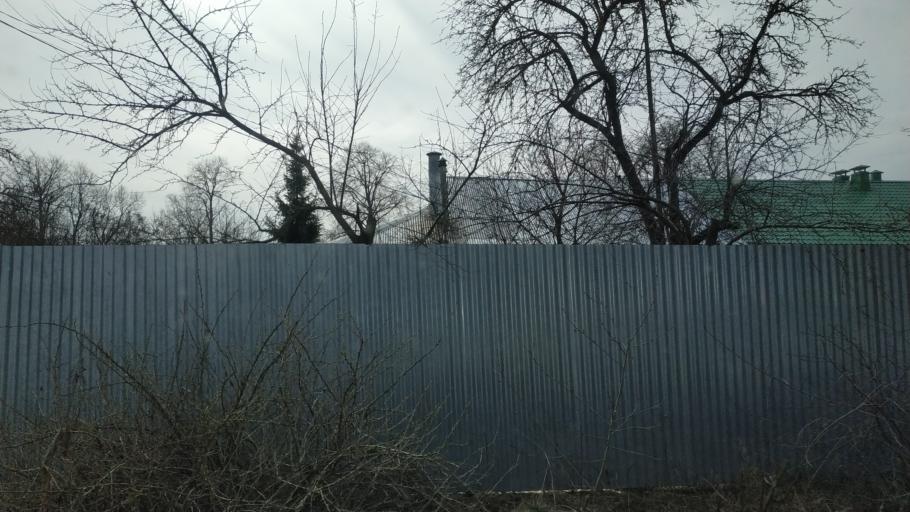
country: RU
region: Moskovskaya
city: Peski
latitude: 55.2584
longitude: 38.7187
